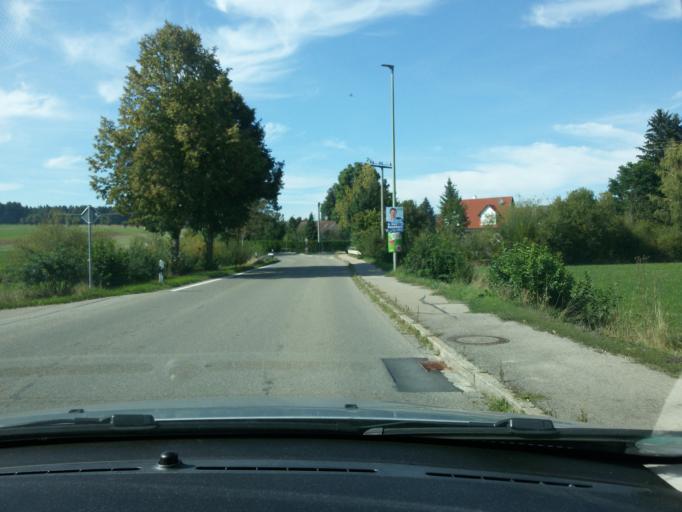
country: DE
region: Bavaria
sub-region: Swabia
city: Mickhausen
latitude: 48.2454
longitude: 10.6384
